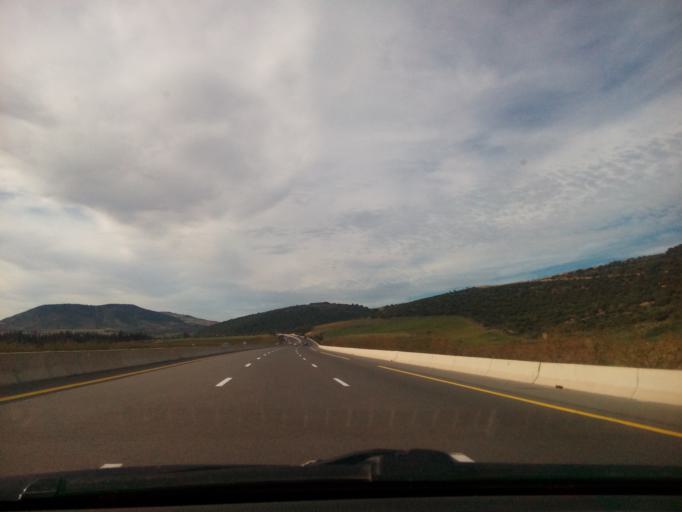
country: DZ
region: Sidi Bel Abbes
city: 'Ain el Berd
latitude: 35.4268
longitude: -0.4644
